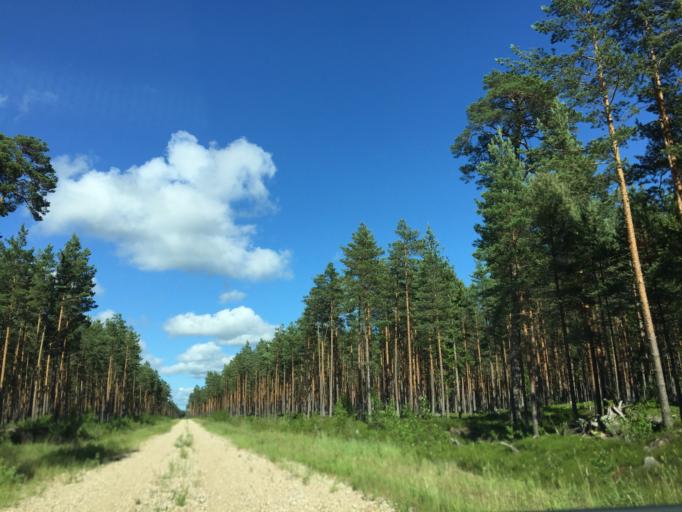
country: LV
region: Ventspils
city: Ventspils
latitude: 57.5299
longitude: 21.7153
